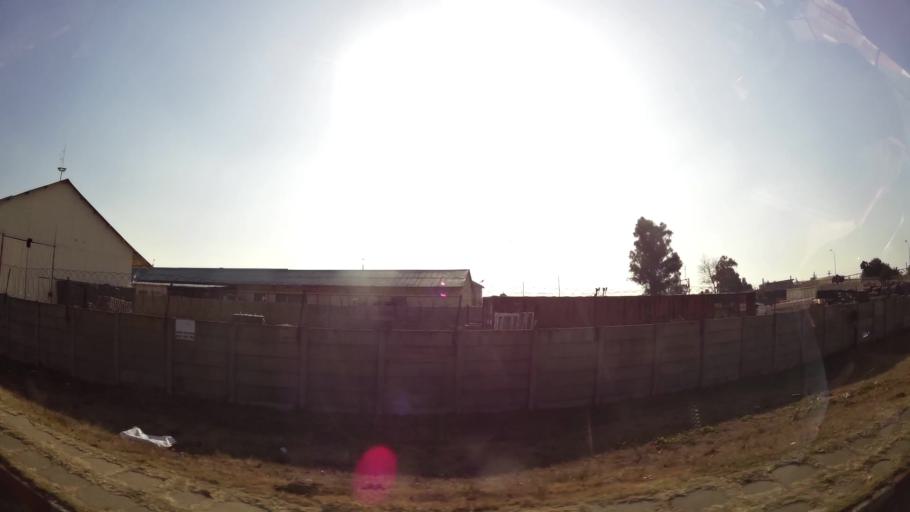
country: ZA
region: Gauteng
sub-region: West Rand District Municipality
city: Randfontein
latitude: -26.1573
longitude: 27.7178
